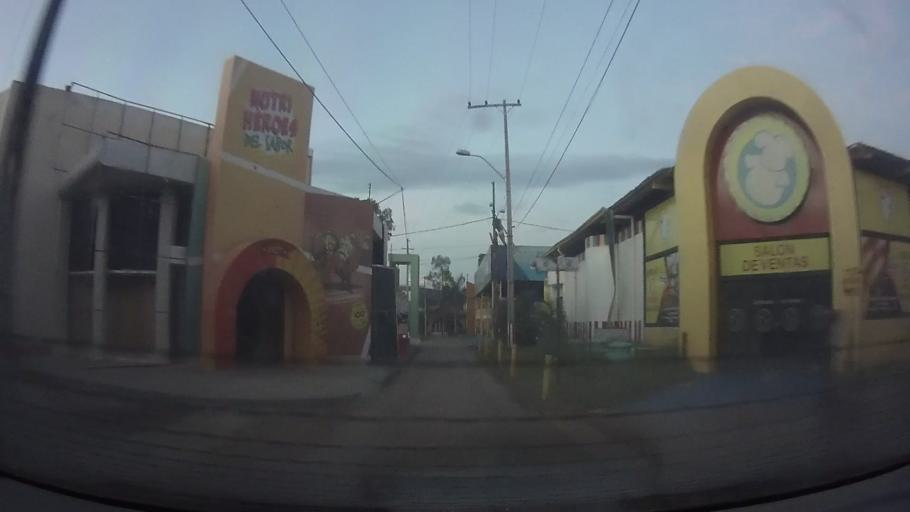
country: PY
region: Central
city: Colonia Mariano Roque Alonso
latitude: -25.2291
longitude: -57.5334
